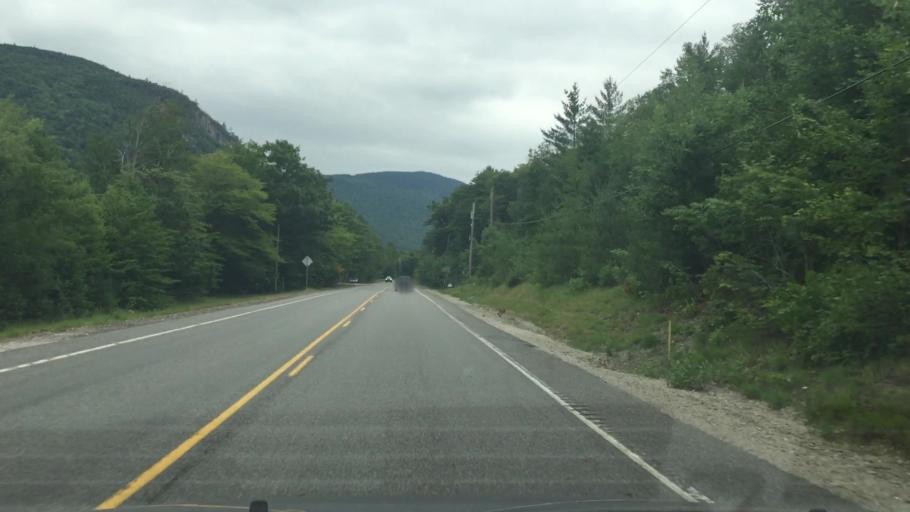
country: US
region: New Hampshire
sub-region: Carroll County
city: North Conway
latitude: 44.1391
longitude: -71.3635
